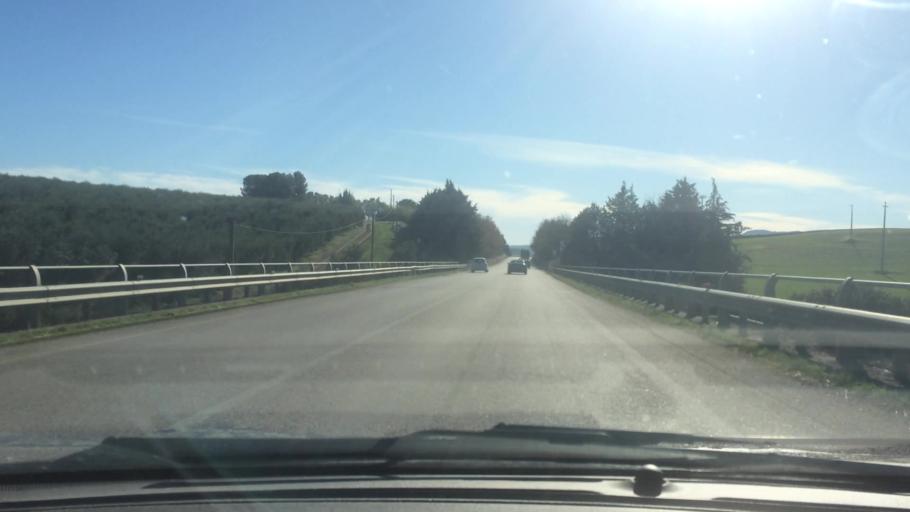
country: IT
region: Basilicate
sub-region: Provincia di Matera
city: Miglionico
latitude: 40.5914
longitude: 16.5738
